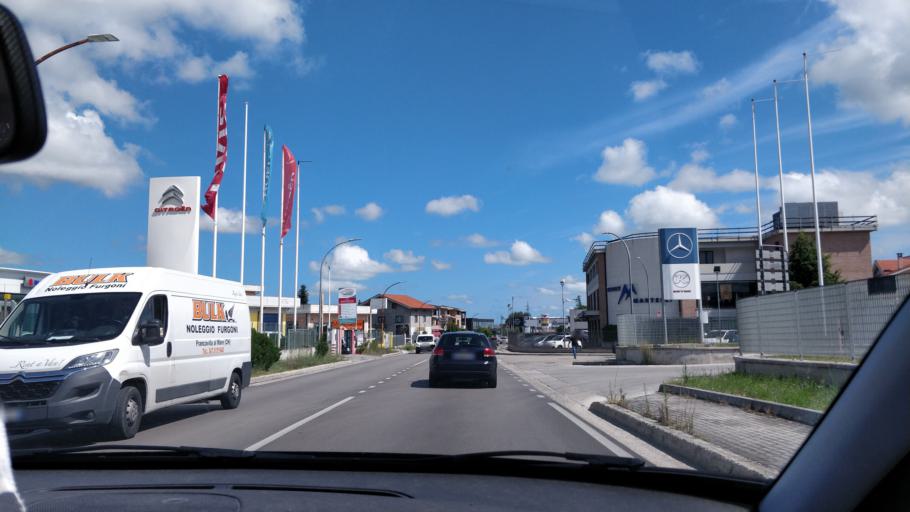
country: IT
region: Abruzzo
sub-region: Provincia di Chieti
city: Lanciano
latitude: 42.2382
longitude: 14.4094
